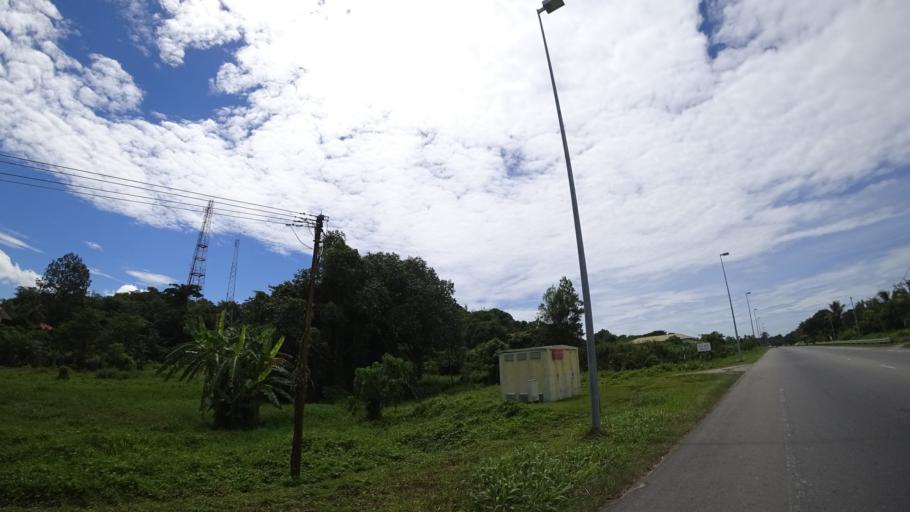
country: BN
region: Brunei and Muara
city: Bandar Seri Begawan
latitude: 4.8216
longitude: 114.8413
